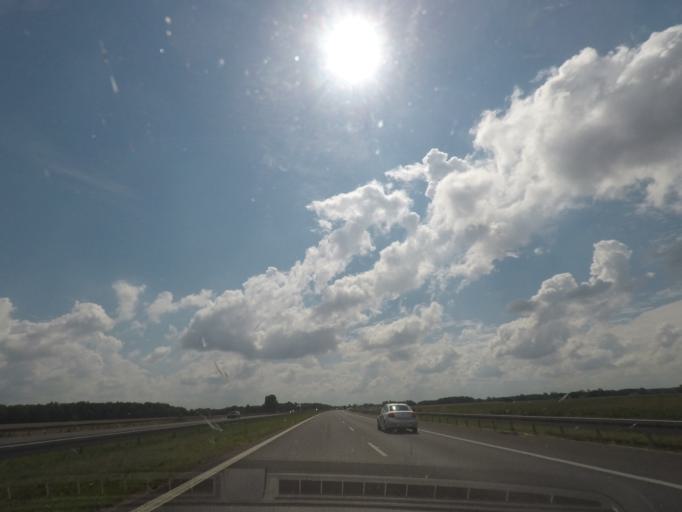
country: PL
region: Lodz Voivodeship
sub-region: Powiat zgierski
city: Strykow
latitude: 51.9524
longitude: 19.6017
